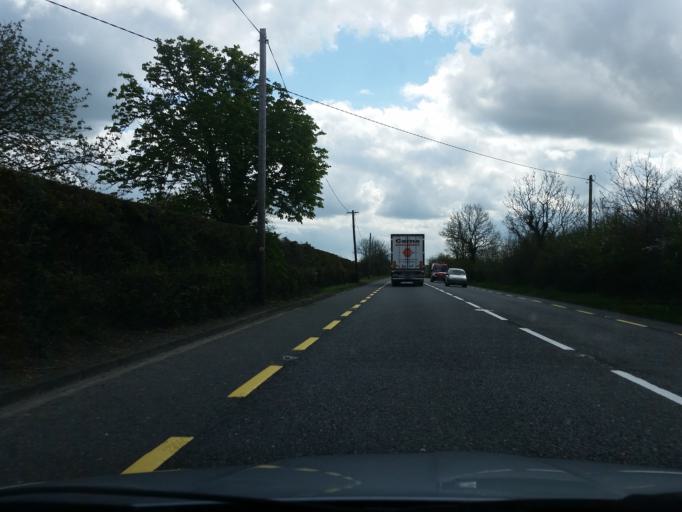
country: IE
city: Kentstown
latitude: 53.5871
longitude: -6.4607
